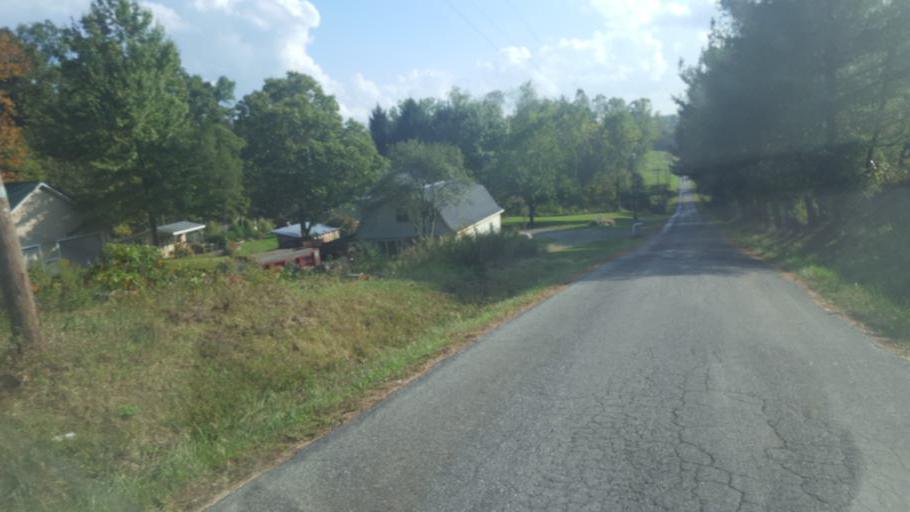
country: US
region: Ohio
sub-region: Holmes County
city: Millersburg
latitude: 40.6335
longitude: -81.8320
